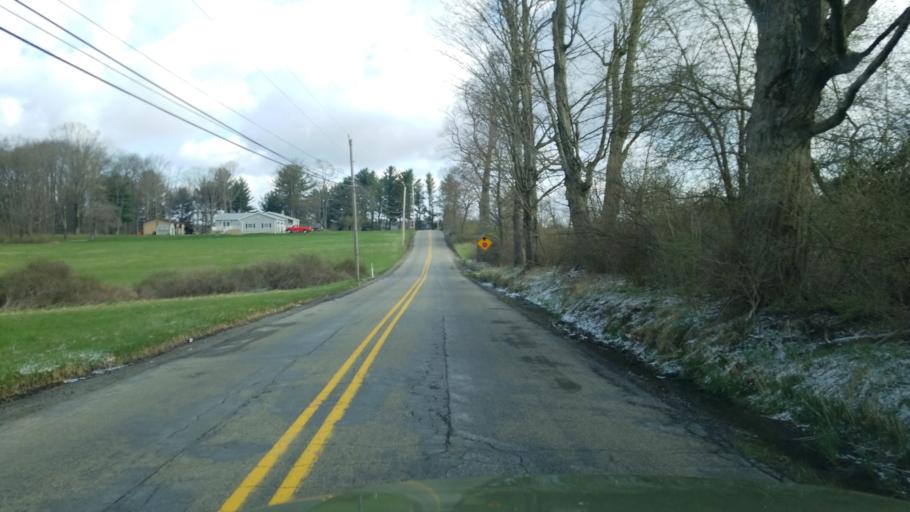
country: US
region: Pennsylvania
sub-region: Jefferson County
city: Brockway
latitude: 41.2729
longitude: -78.8430
